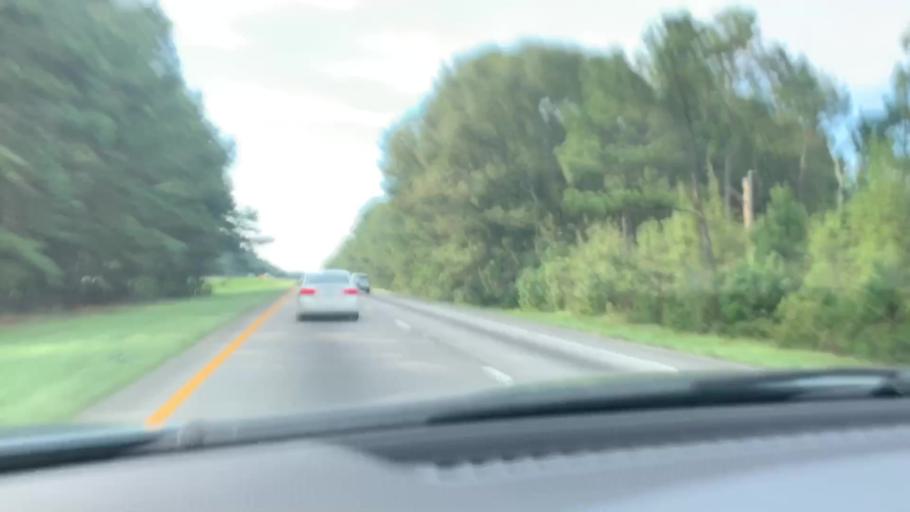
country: US
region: South Carolina
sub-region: Orangeburg County
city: Brookdale
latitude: 33.4386
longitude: -80.7036
